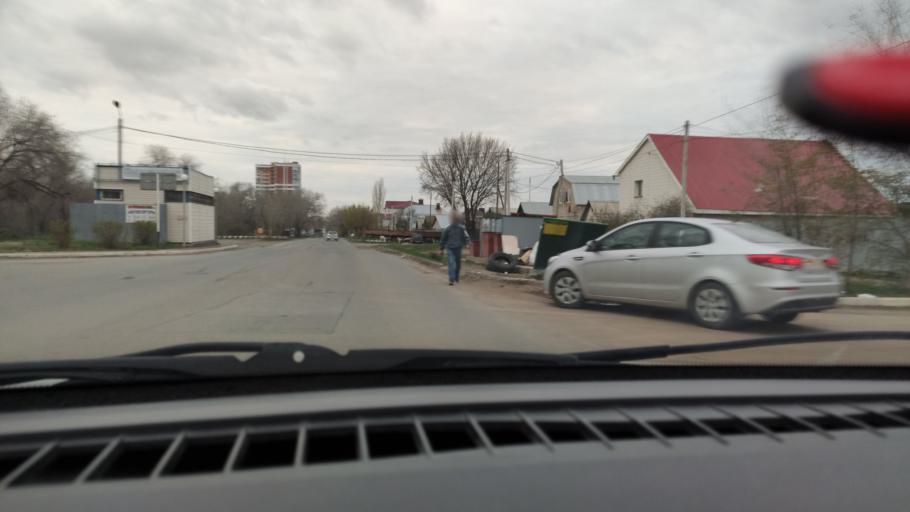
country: RU
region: Orenburg
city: Orenburg
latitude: 51.7873
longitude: 55.1442
